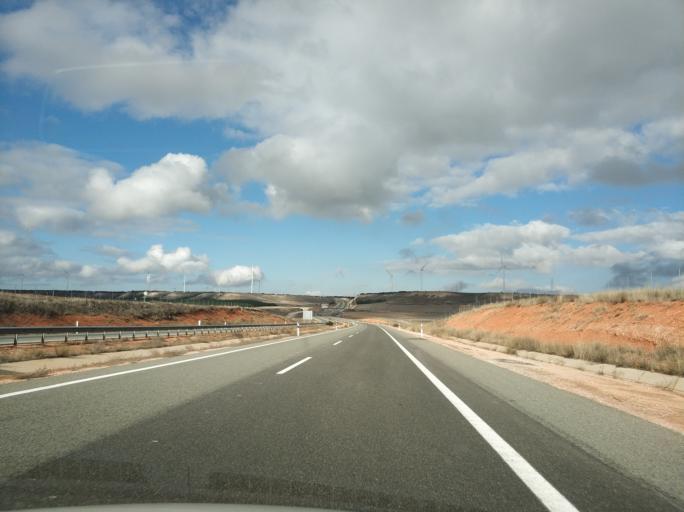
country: ES
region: Castille and Leon
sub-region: Provincia de Soria
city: Alcubilla de las Penas
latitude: 41.2735
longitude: -2.4745
